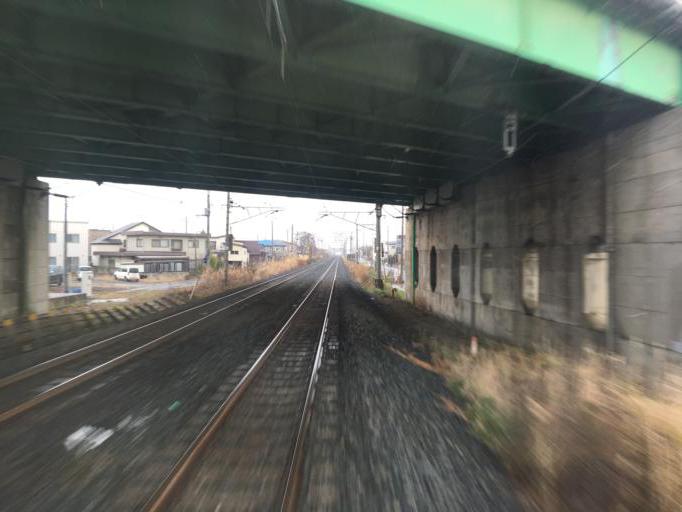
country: JP
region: Aomori
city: Aomori Shi
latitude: 40.8273
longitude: 140.8042
